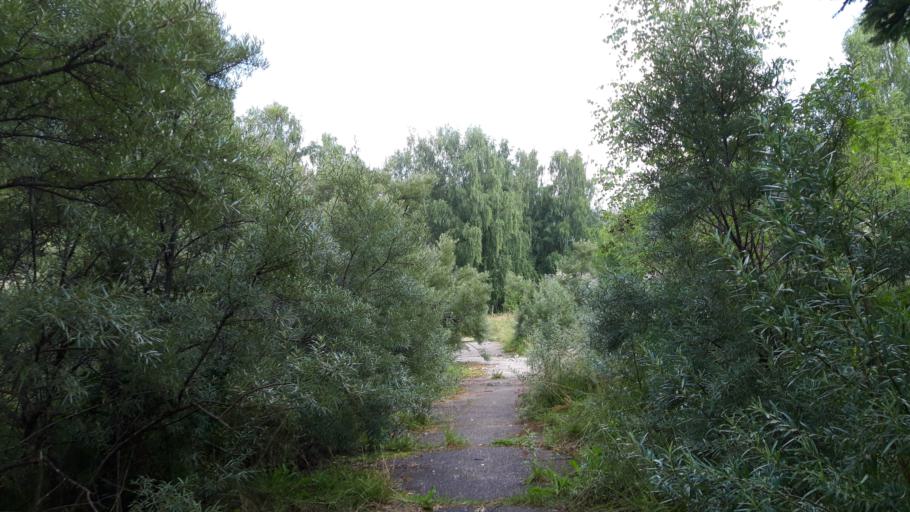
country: RU
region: Tverskaya
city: Konakovo
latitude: 56.6658
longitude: 36.6830
